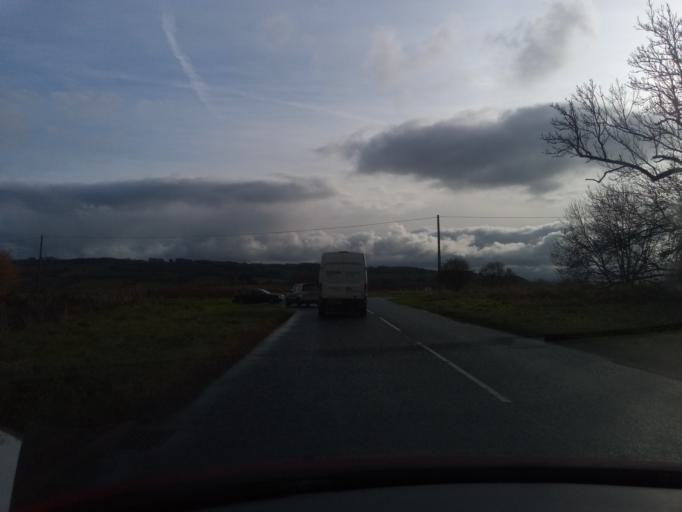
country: GB
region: England
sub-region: Northumberland
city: Wall
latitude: 55.0370
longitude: -2.1366
